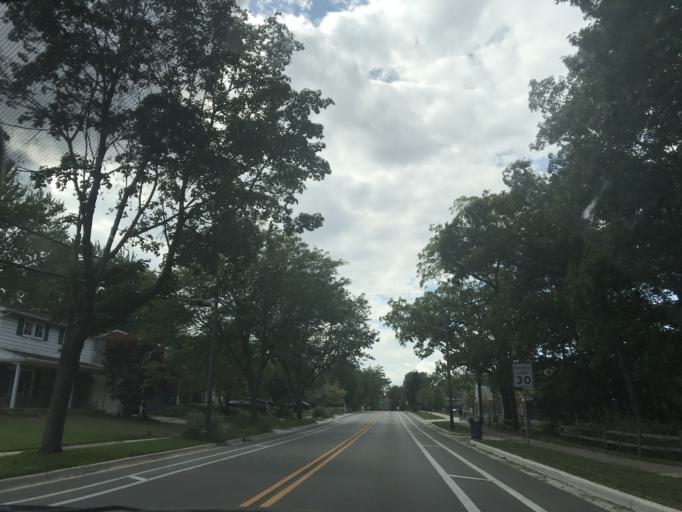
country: US
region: Michigan
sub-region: Washtenaw County
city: Ann Arbor
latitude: 42.2683
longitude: -83.7643
